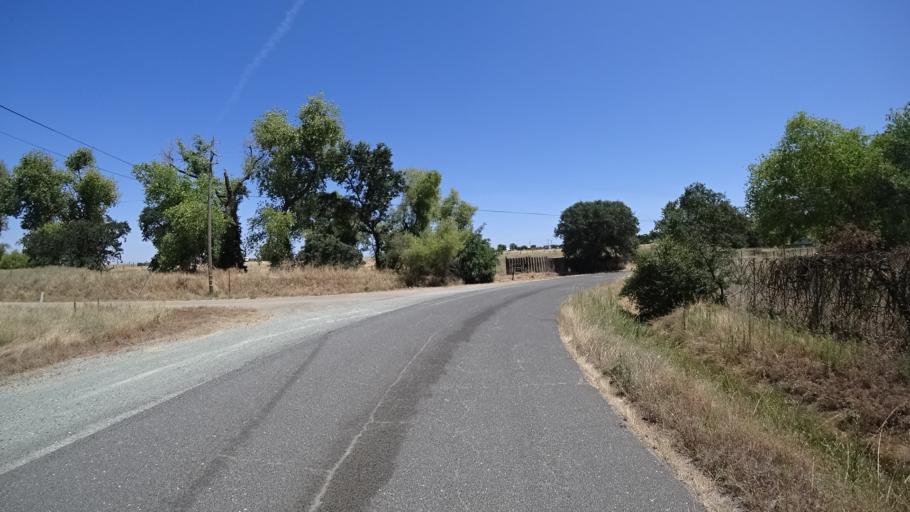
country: US
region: California
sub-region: San Joaquin County
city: Dogtown
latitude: 38.1955
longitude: -120.9820
